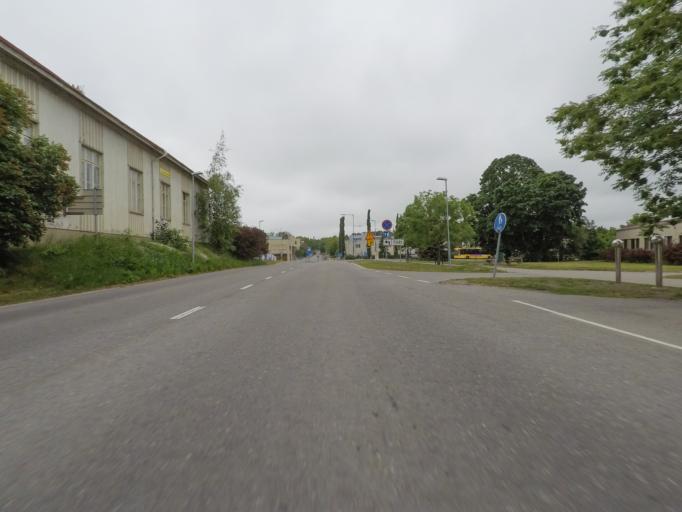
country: FI
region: Varsinais-Suomi
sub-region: Turku
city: Naantali
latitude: 60.4680
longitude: 22.0284
